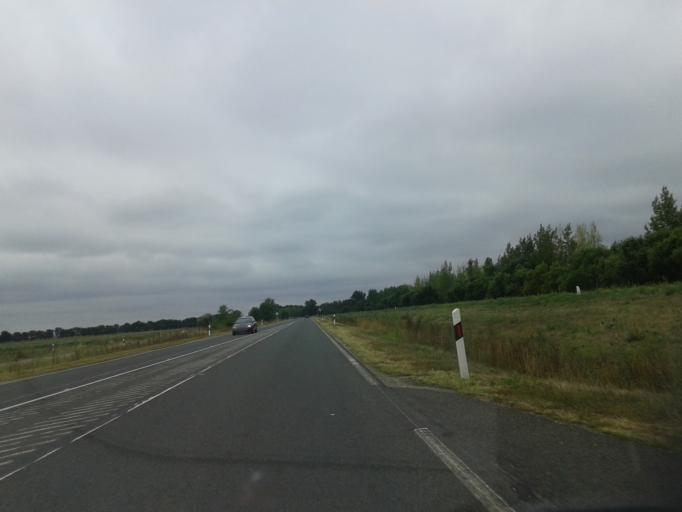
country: HU
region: Bacs-Kiskun
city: Harta
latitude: 46.7292
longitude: 19.0162
